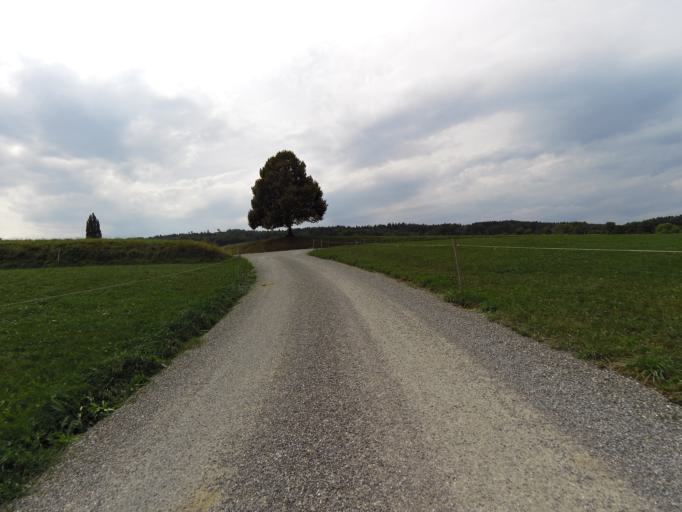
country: CH
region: Thurgau
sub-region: Kreuzlingen District
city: Ermatingen
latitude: 47.6603
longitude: 9.0629
